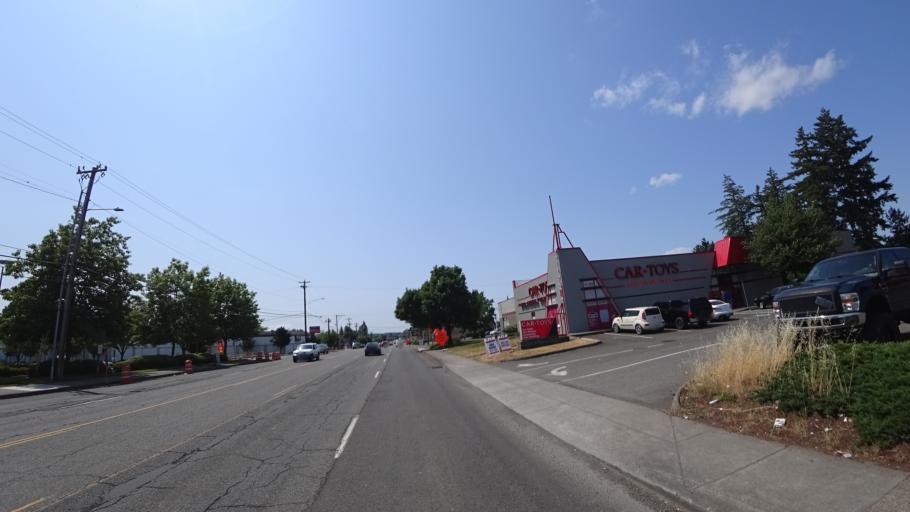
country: US
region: Oregon
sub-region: Multnomah County
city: Lents
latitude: 45.4492
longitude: -122.5791
